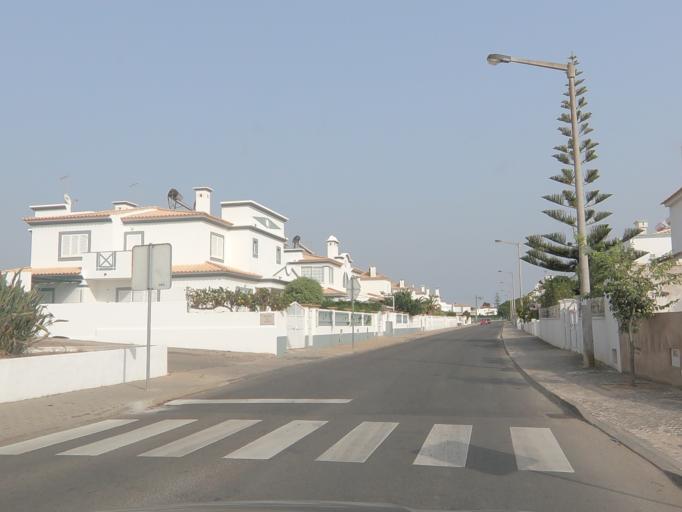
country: PT
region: Faro
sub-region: Albufeira
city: Guia
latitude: 37.0831
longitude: -8.3100
